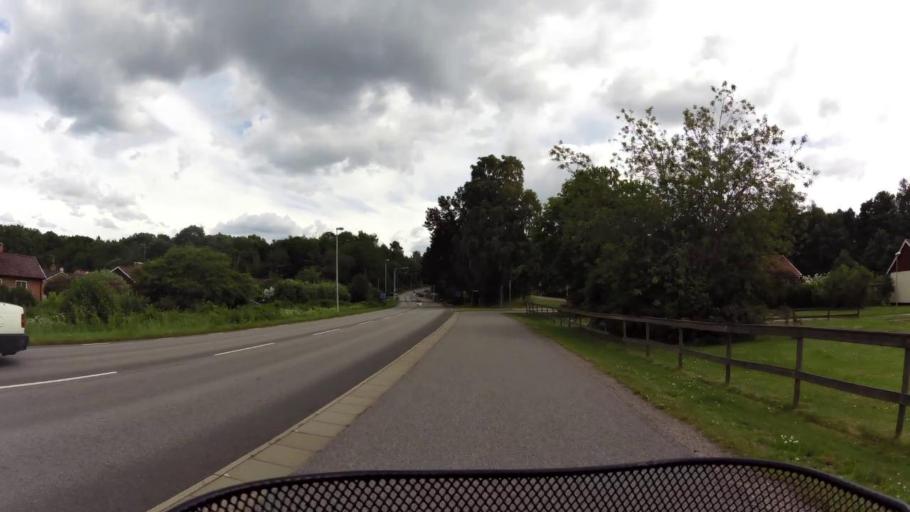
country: SE
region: OEstergoetland
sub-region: Linkopings Kommun
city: Malmslatt
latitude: 58.4134
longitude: 15.5237
